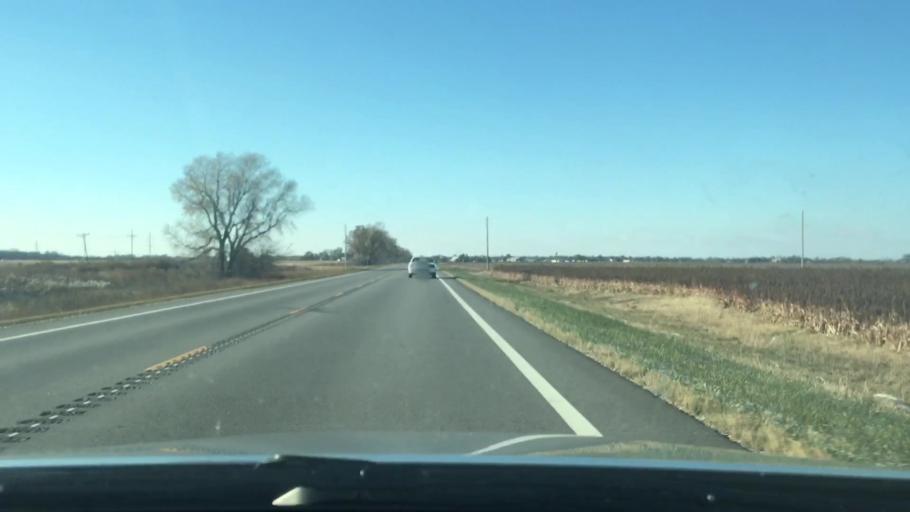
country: US
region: Kansas
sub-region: Reno County
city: Nickerson
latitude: 38.1289
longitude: -98.0567
